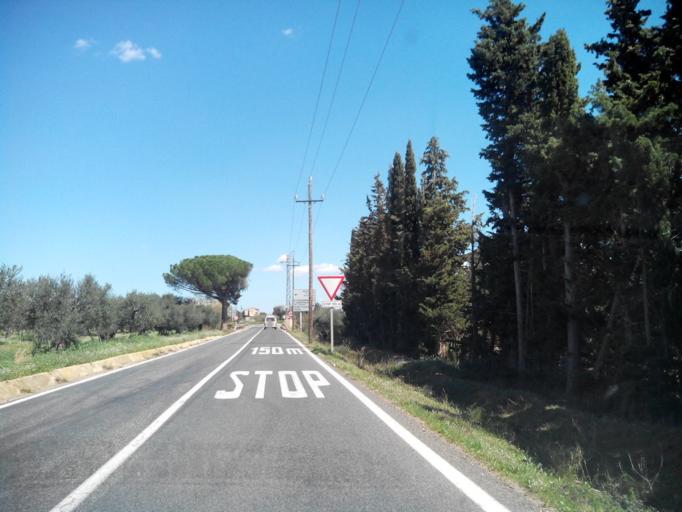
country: ES
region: Catalonia
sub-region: Provincia de Tarragona
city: Riudecanyes
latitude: 41.0959
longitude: 0.9714
